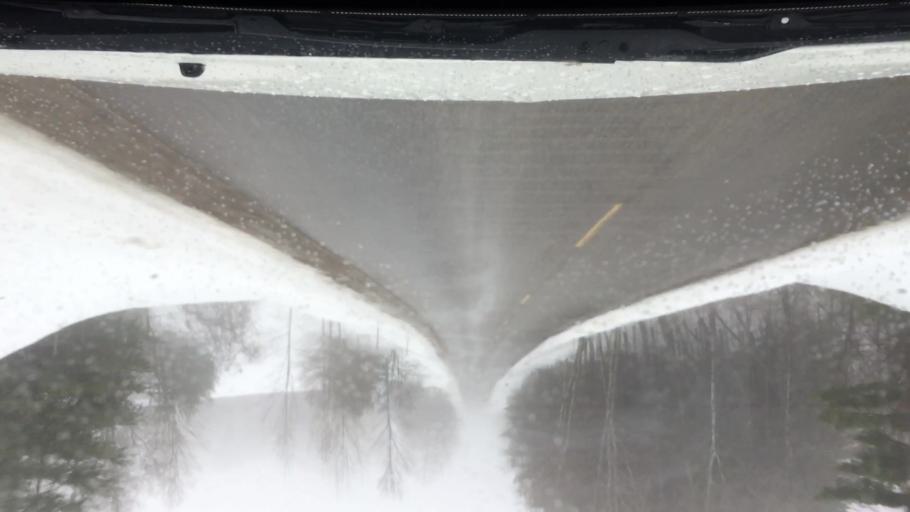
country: US
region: Michigan
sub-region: Charlevoix County
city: East Jordan
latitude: 45.1278
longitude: -85.1802
